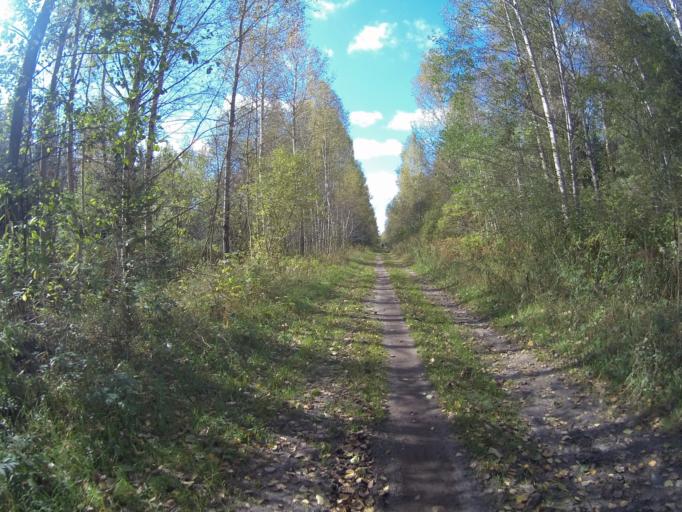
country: RU
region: Vladimir
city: Raduzhnyy
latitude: 55.9383
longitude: 40.2296
